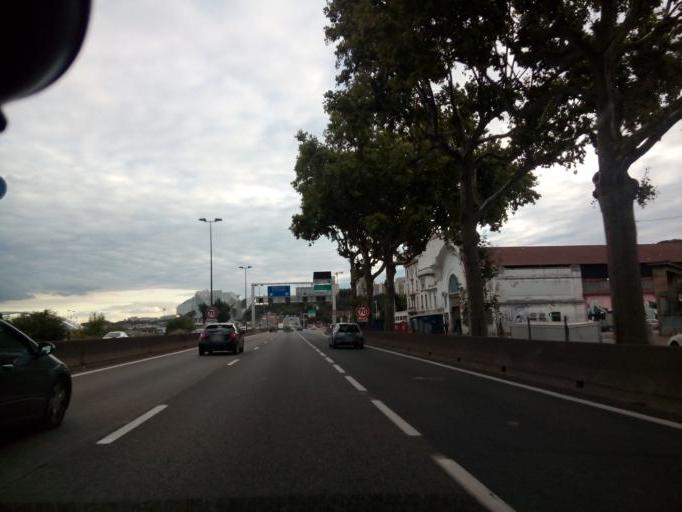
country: FR
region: Rhone-Alpes
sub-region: Departement du Rhone
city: La Mulatiere
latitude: 45.7377
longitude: 4.8212
